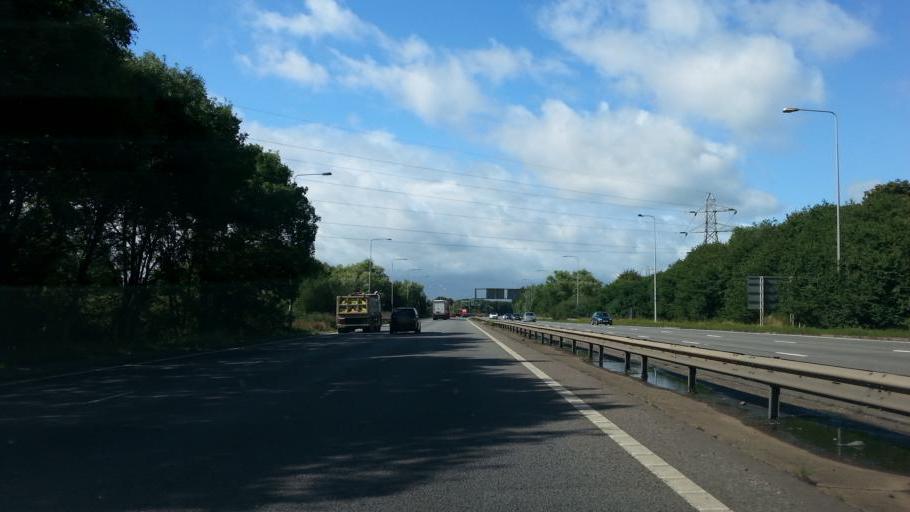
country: GB
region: England
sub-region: Northamptonshire
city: Northampton
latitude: 52.2404
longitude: -0.8443
